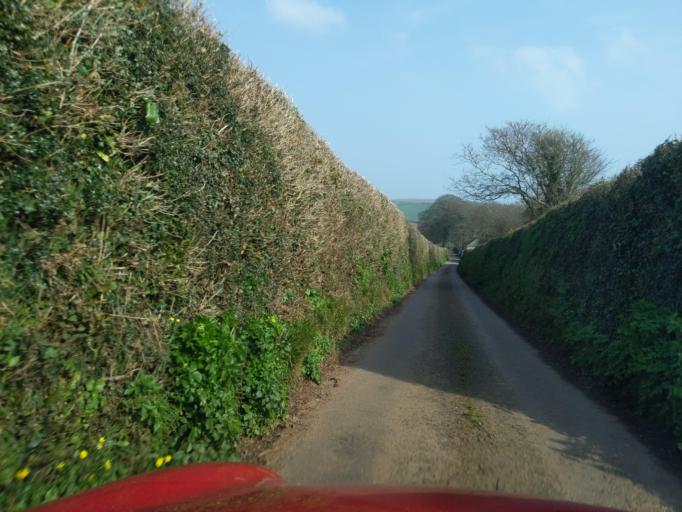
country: GB
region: England
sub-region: Devon
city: Kingsbridge
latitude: 50.2870
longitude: -3.7312
